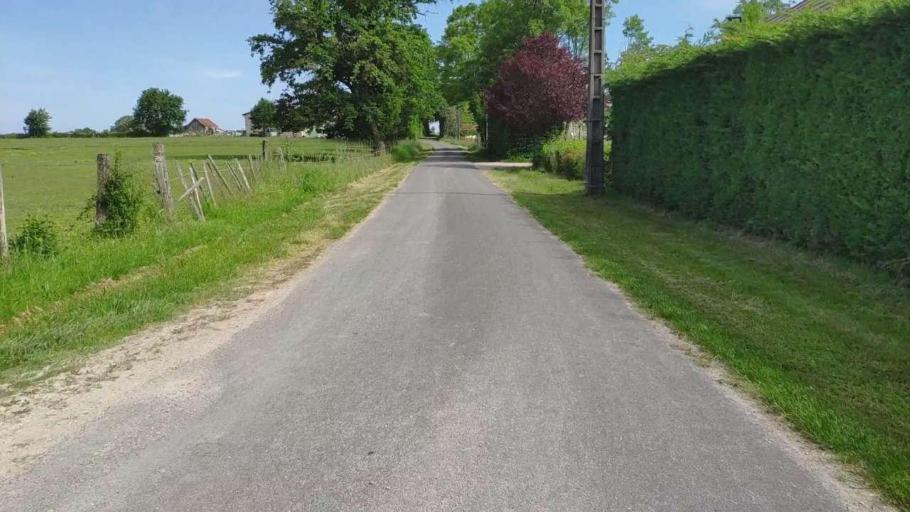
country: FR
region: Franche-Comte
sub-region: Departement du Jura
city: Bletterans
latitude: 46.6801
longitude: 5.4082
